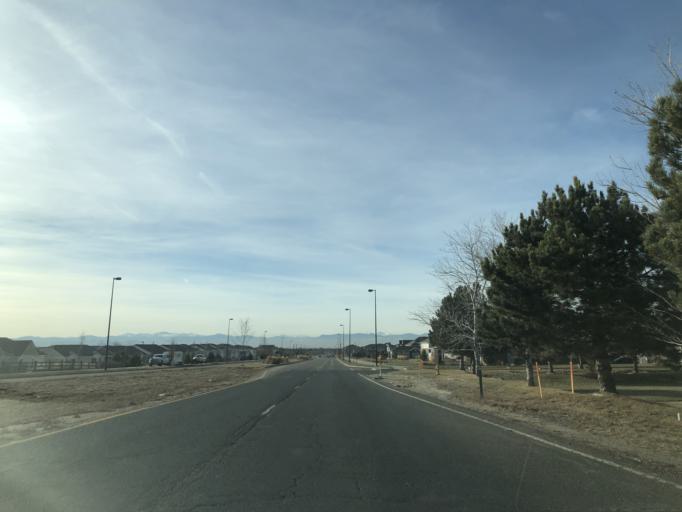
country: US
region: Colorado
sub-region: Adams County
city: Aurora
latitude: 39.7986
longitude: -104.7571
